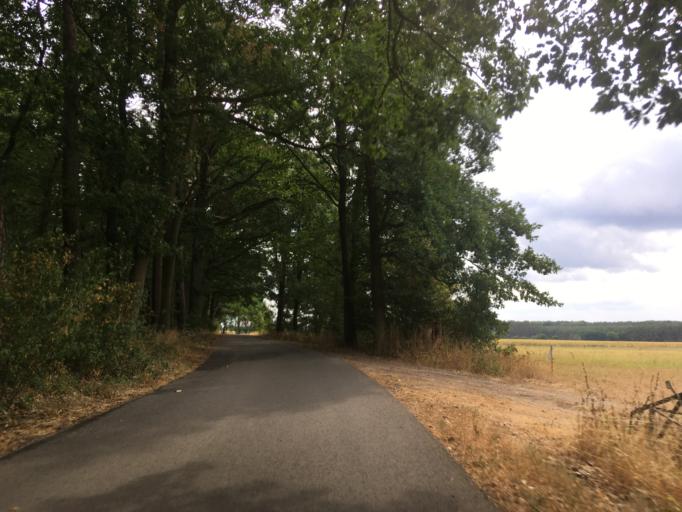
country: DE
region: Brandenburg
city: Chorin
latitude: 52.9068
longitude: 13.8553
